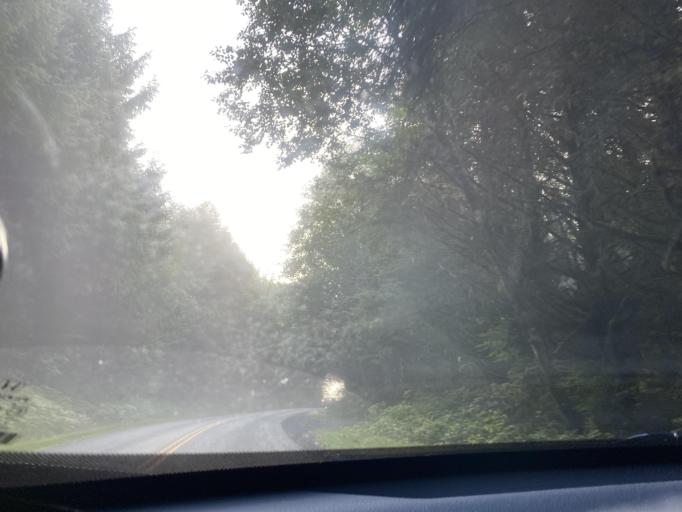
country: US
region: Washington
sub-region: Clallam County
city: Forks
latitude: 47.8100
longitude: -124.0839
